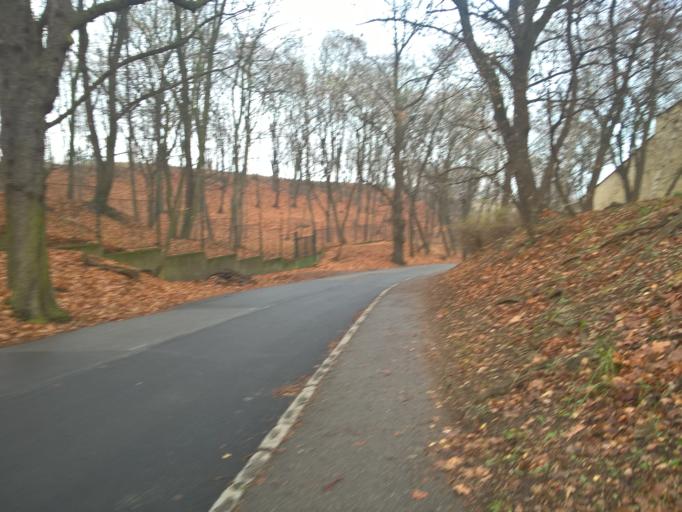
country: CZ
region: Praha
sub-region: Praha 1
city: Mala Strana
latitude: 50.0841
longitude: 14.3899
